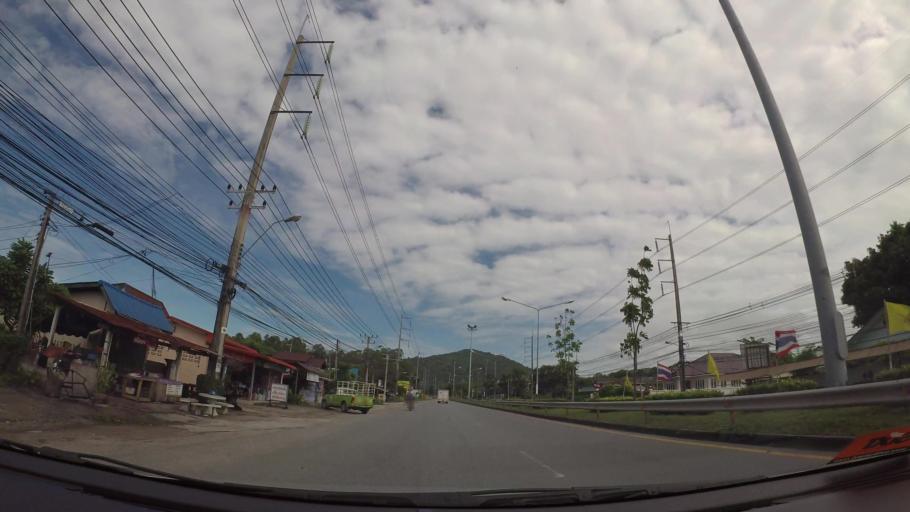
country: TH
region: Rayong
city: Ban Chang
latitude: 12.7466
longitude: 101.1113
